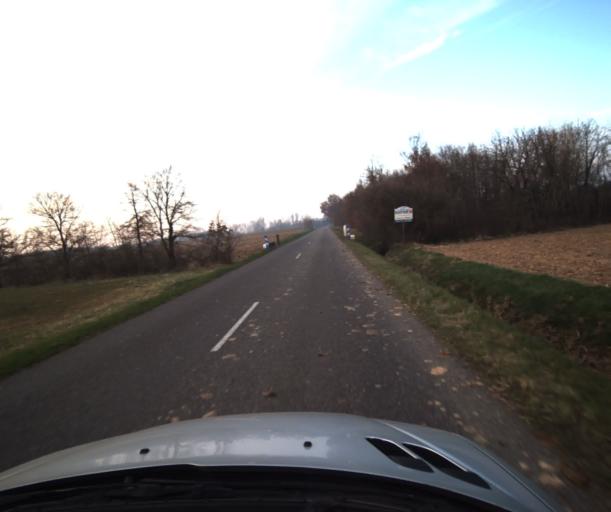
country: FR
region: Midi-Pyrenees
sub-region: Departement du Tarn-et-Garonne
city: Labastide-Saint-Pierre
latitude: 43.8977
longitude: 1.3711
